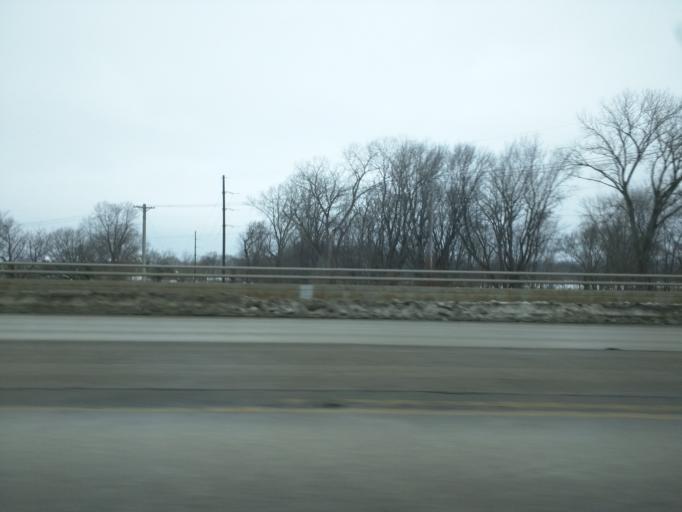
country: US
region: Wisconsin
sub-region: La Crosse County
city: La Crosse
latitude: 43.8199
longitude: -91.2491
